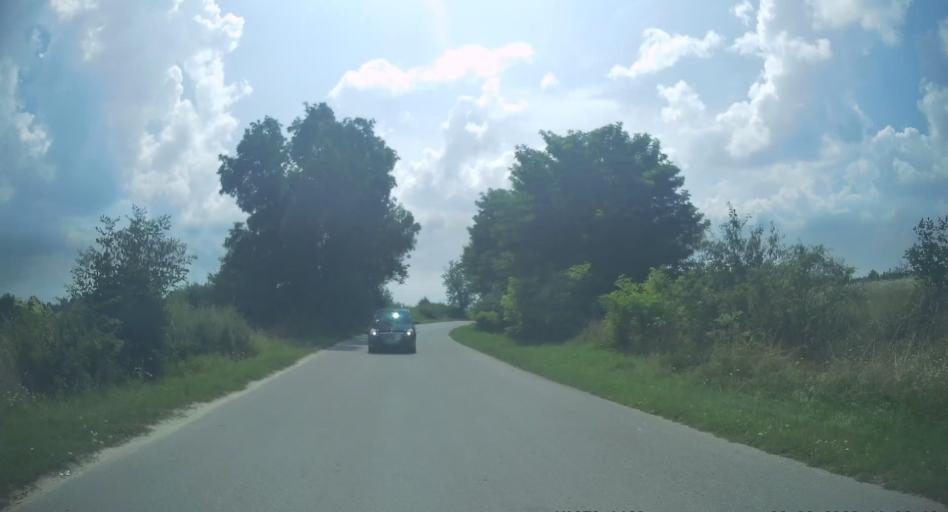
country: PL
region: Swietokrzyskie
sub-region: Powiat kielecki
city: Checiny
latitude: 50.7936
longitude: 20.4542
